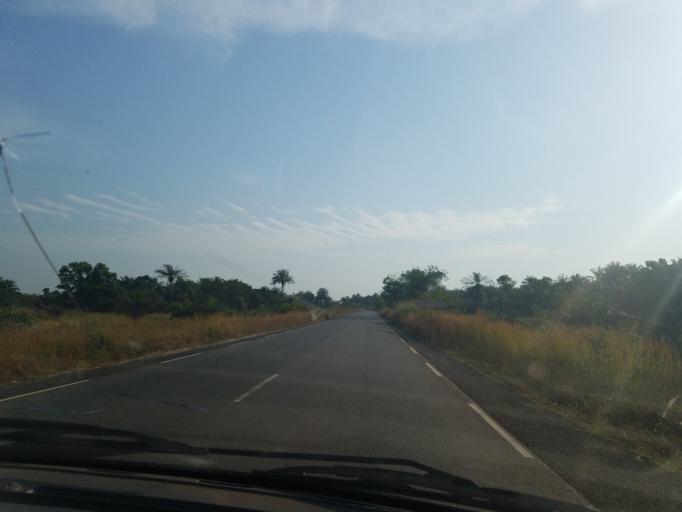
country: GN
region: Boke
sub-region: Boke Prefecture
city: Sangueya
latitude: 10.4967
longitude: -14.4058
